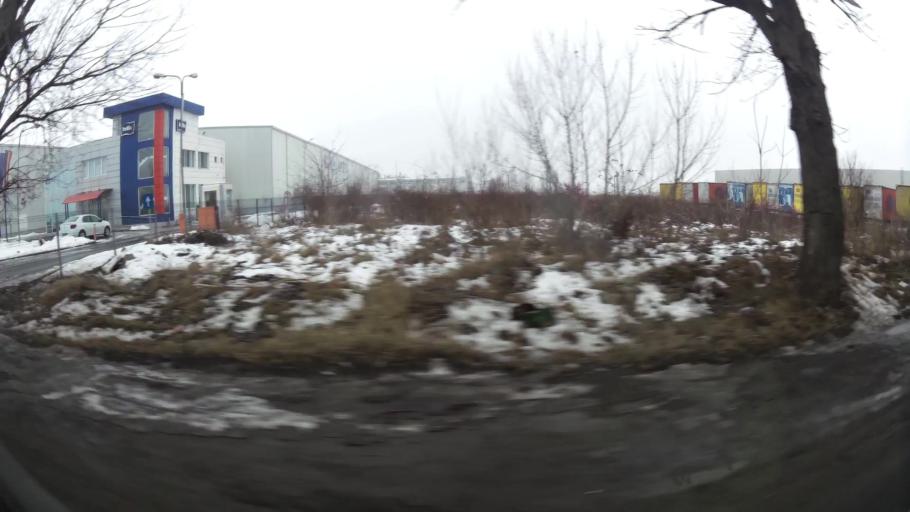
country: RO
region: Ilfov
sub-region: Comuna Bragadiru
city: Bragadiru
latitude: 44.3971
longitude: 25.9814
